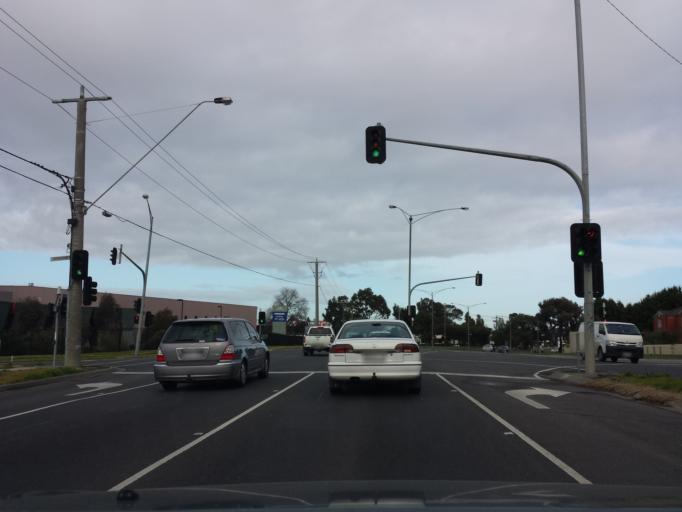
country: AU
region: Victoria
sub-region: Knox
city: Knoxfield
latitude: -37.8962
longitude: 145.2474
